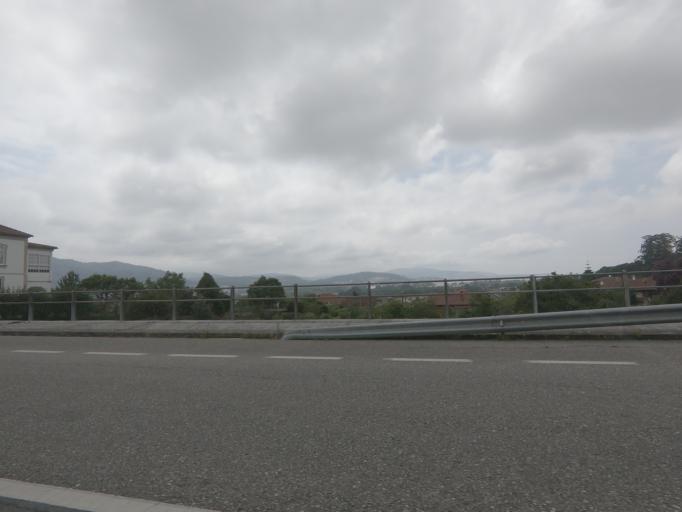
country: ES
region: Galicia
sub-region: Provincia de Pontevedra
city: O Rosal
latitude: 41.9313
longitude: -8.8008
